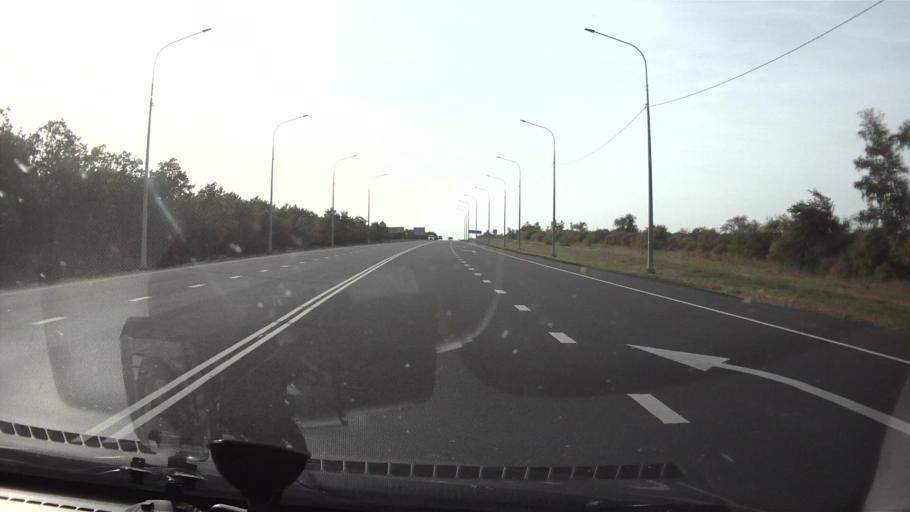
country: RU
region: Saratov
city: Yelshanka
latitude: 51.8203
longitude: 46.3533
